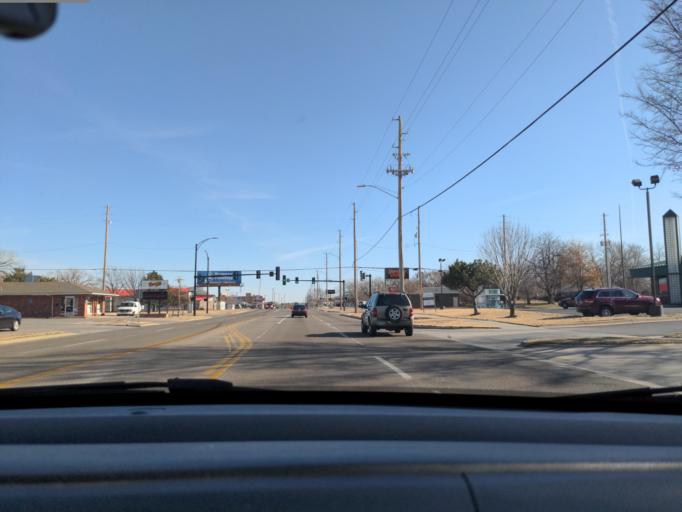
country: US
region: Kansas
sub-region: Sedgwick County
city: Wichita
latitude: 37.6948
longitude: -97.3815
